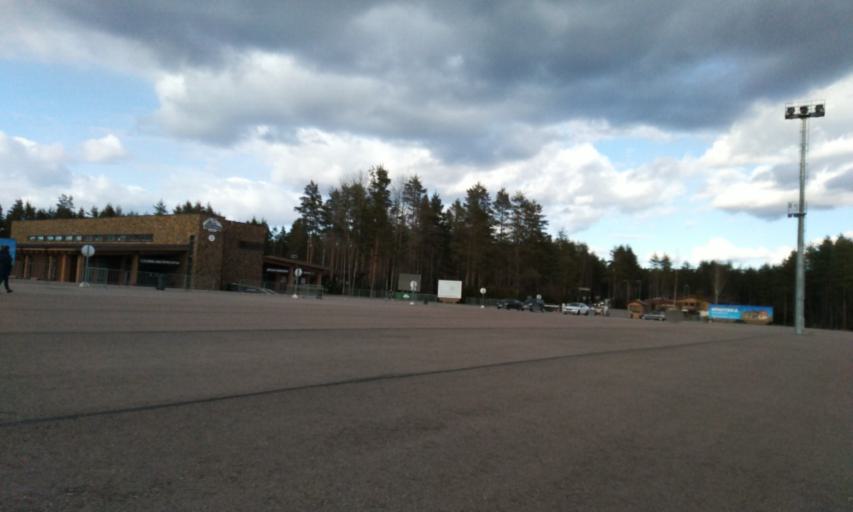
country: RU
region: Leningrad
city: Novoye Devyatkino
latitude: 60.1263
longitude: 30.4448
